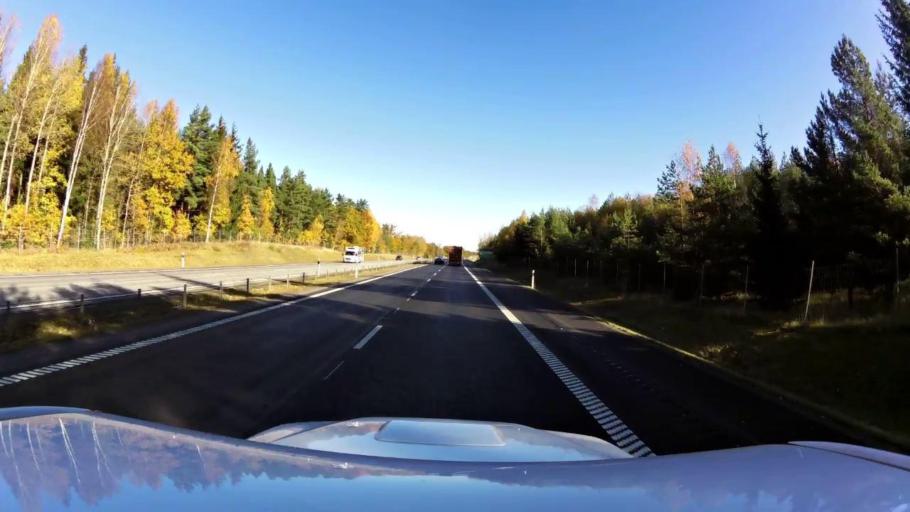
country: SE
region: OEstergoetland
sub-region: Linkopings Kommun
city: Malmslatt
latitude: 58.4234
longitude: 15.4919
